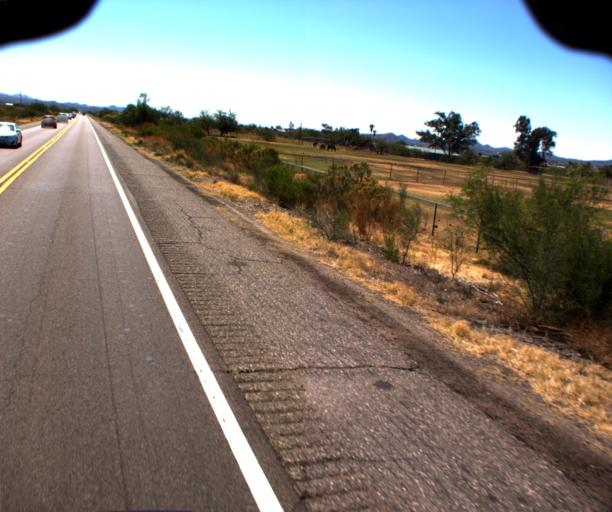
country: US
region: Arizona
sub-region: Maricopa County
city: Wickenburg
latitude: 34.0106
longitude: -112.7872
